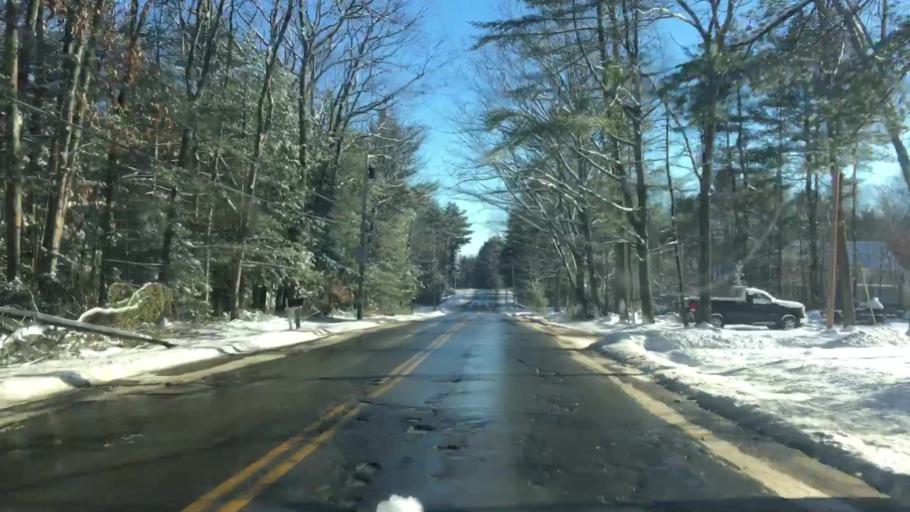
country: US
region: Maine
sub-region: Androscoggin County
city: Lisbon Falls
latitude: 43.9270
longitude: -70.0477
